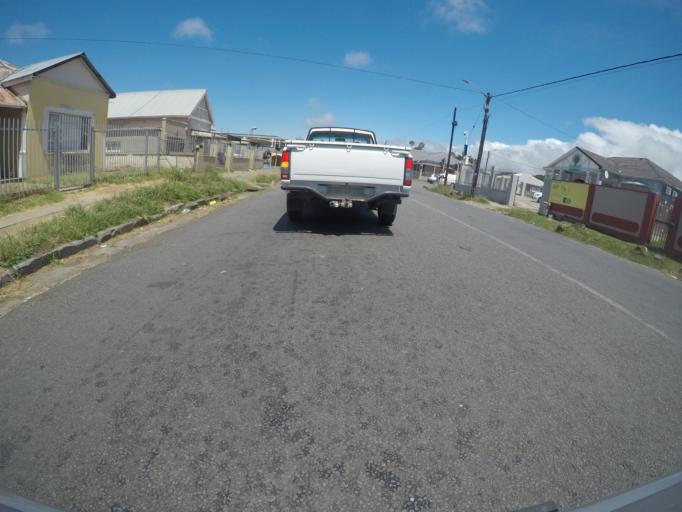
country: ZA
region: Eastern Cape
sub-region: Buffalo City Metropolitan Municipality
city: East London
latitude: -33.0015
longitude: 27.9061
